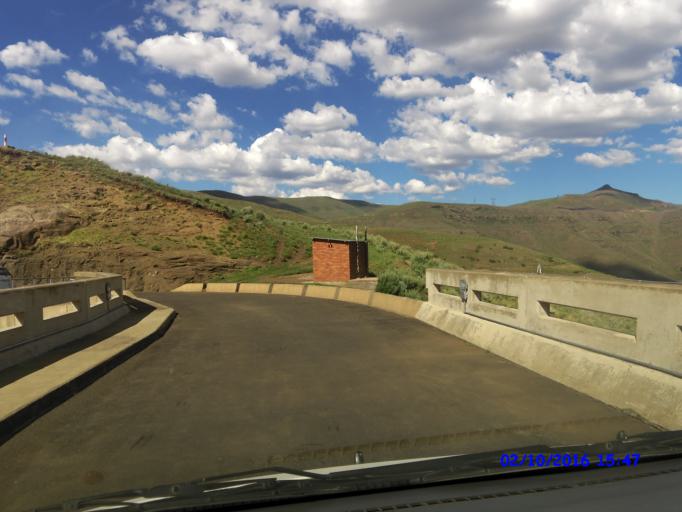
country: LS
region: Maseru
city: Nako
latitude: -29.4556
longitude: 28.0978
